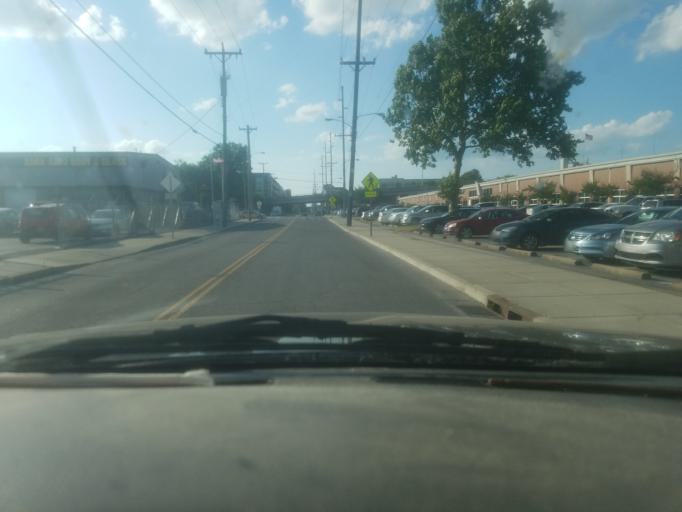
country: US
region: Tennessee
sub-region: Davidson County
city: Nashville
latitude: 36.1737
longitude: -86.7825
